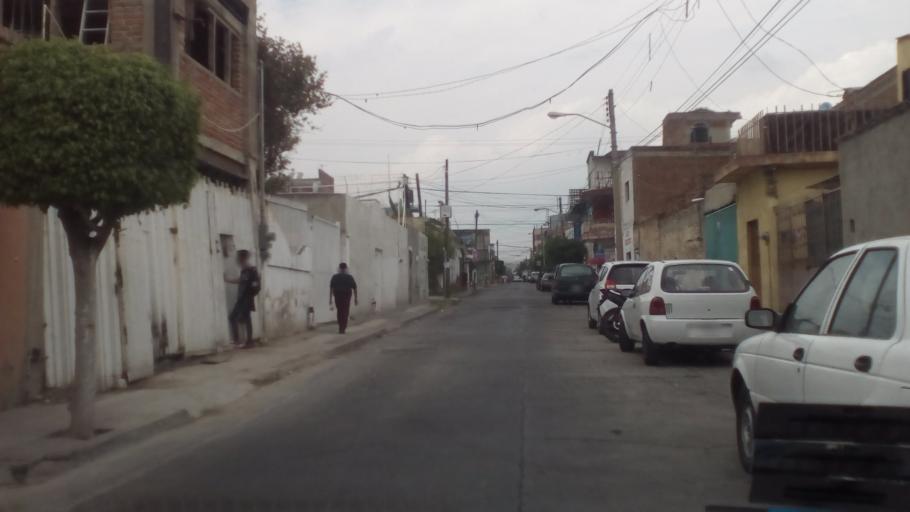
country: MX
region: Guanajuato
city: Leon
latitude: 21.1239
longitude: -101.6898
